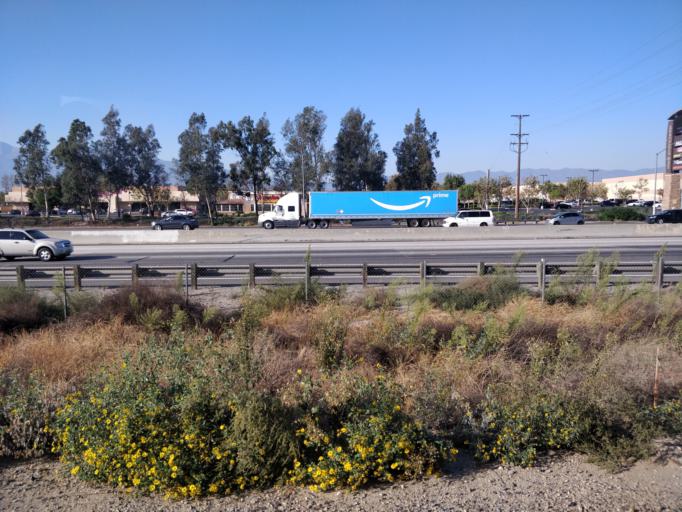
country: US
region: California
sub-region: San Bernardino County
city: Fontana
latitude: 34.0667
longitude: -117.4406
